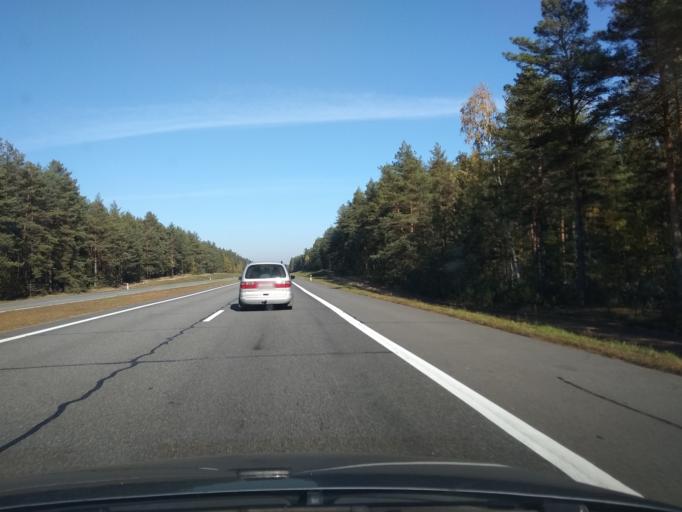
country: BY
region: Brest
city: Baranovichi
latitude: 53.0073
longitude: 25.7735
